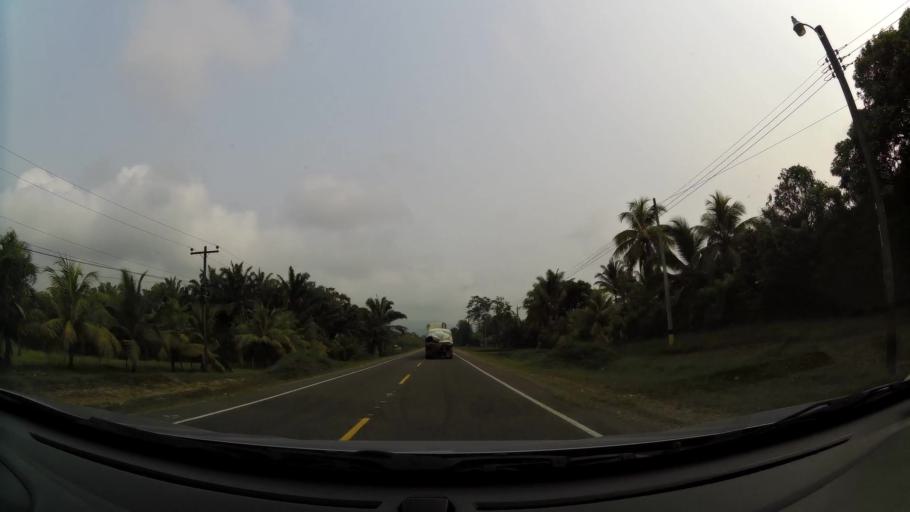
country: HN
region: Atlantida
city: Mezapa
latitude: 15.6176
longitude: -87.6156
